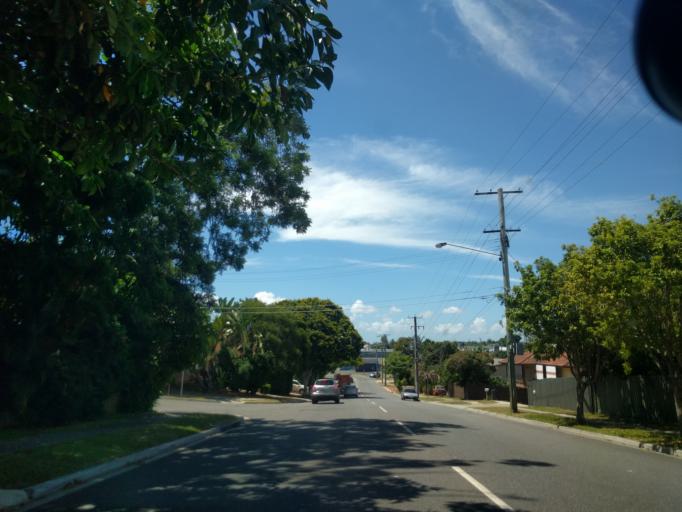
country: AU
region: Queensland
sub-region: Brisbane
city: Chermside West
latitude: -27.3666
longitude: 153.0159
